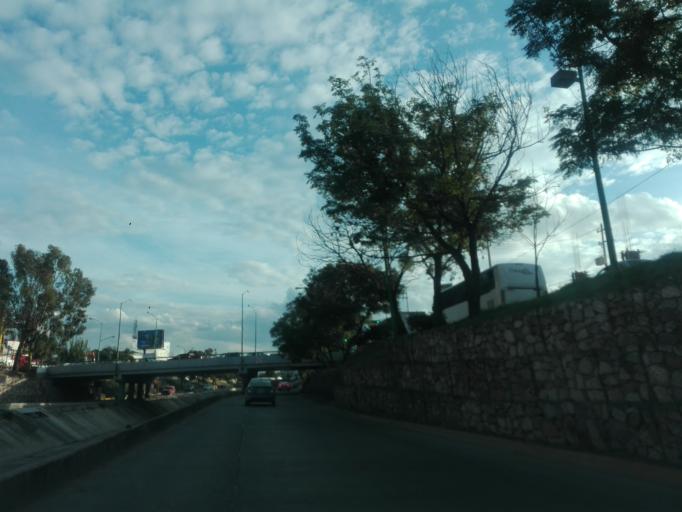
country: MX
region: Guanajuato
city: Leon
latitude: 21.1359
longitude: -101.6789
